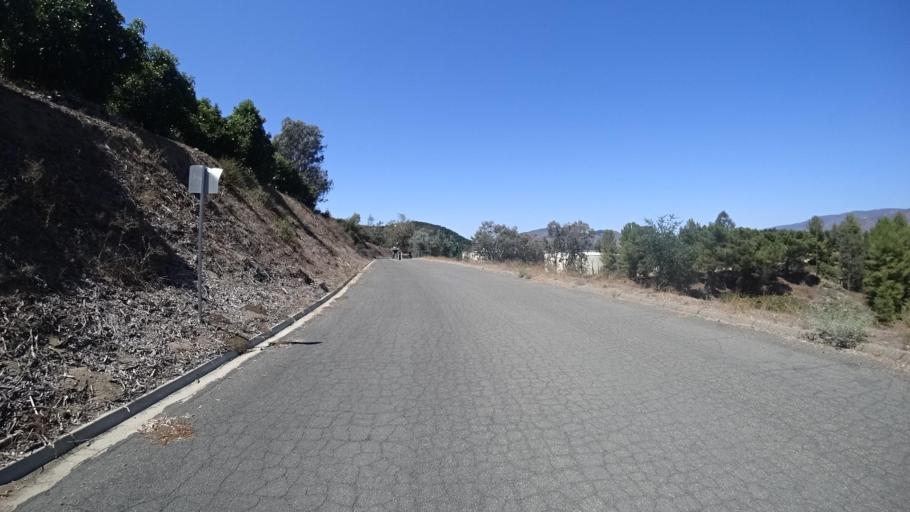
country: US
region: California
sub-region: San Diego County
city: Valley Center
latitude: 33.3007
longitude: -116.9926
